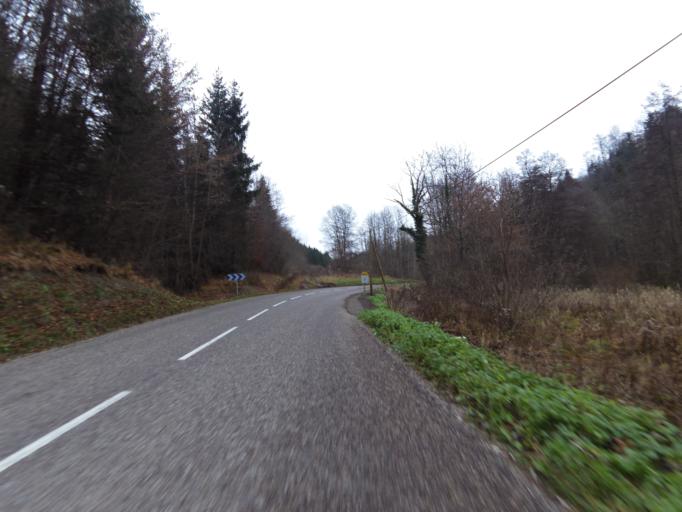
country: FR
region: Alsace
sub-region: Departement du Haut-Rhin
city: Ferrette
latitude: 47.4392
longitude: 7.3191
